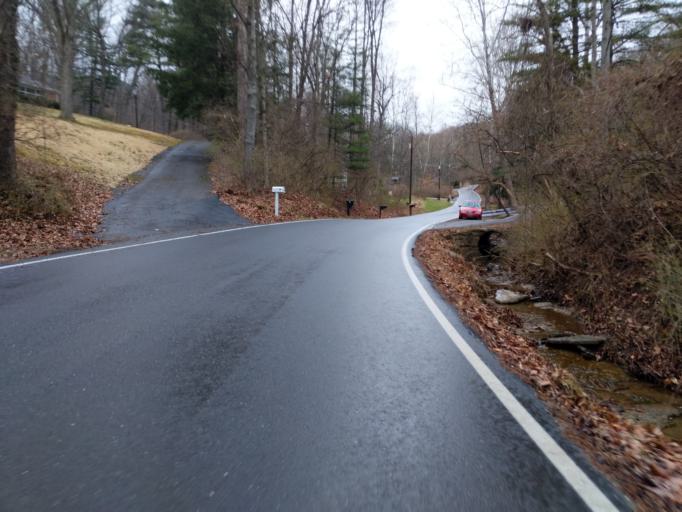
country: US
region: Ohio
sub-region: Athens County
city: Athens
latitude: 39.3414
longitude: -82.0887
